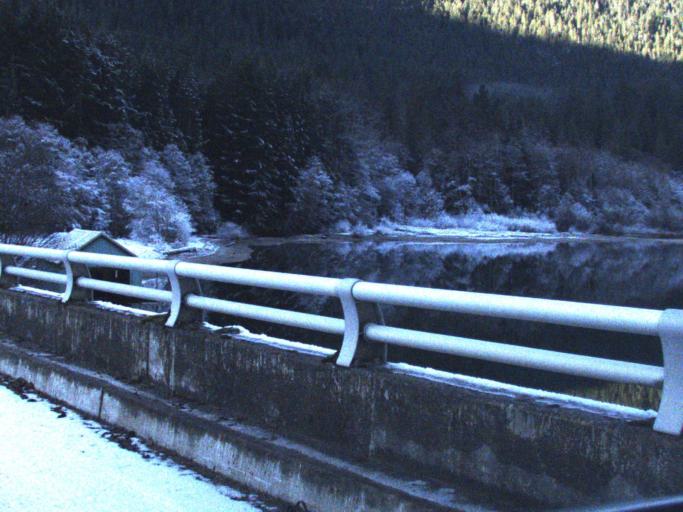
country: US
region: Washington
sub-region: Snohomish County
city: Darrington
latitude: 48.6911
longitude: -121.0955
